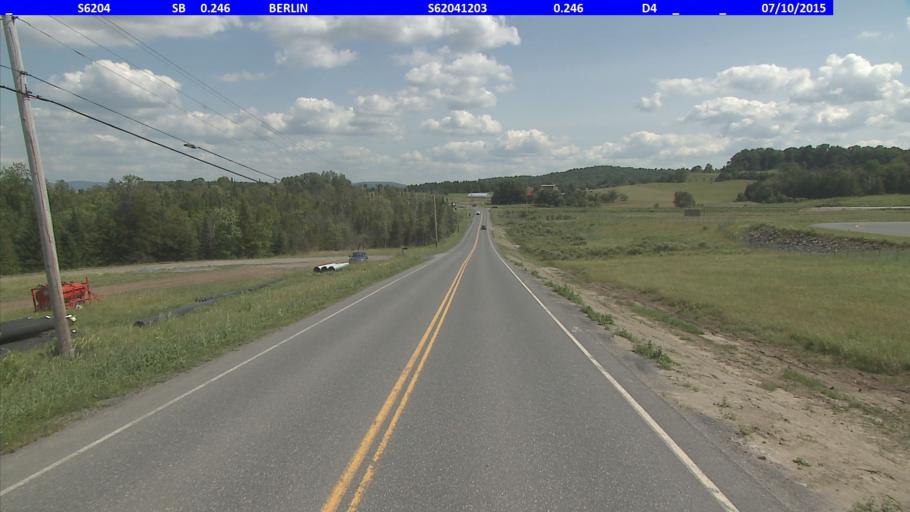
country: US
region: Vermont
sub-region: Washington County
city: South Barre
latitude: 44.1960
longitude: -72.5579
